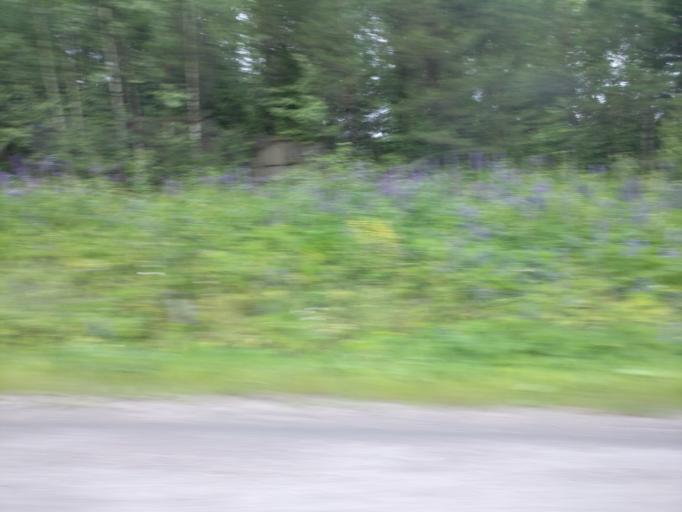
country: FI
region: Northern Savo
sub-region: Varkaus
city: Leppaevirta
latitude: 62.4474
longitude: 27.7945
